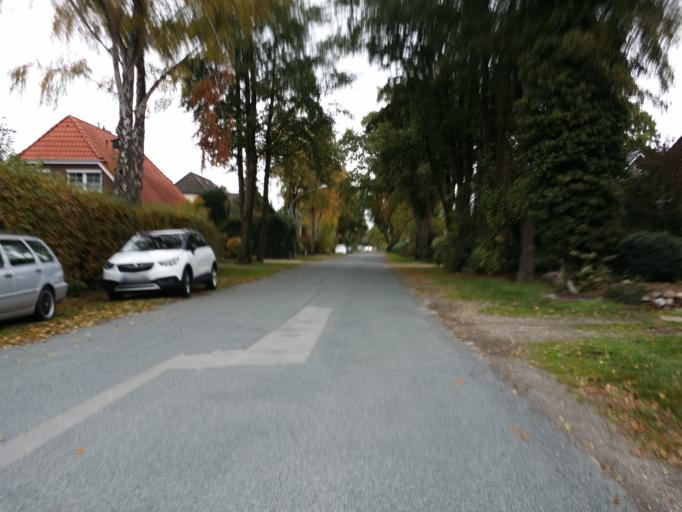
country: DE
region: Lower Saxony
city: Delmenhorst
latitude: 53.0351
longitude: 8.6565
